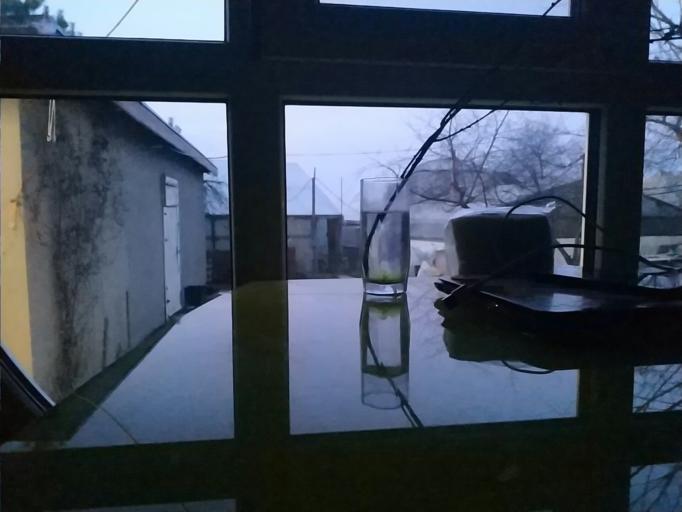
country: RU
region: Republic of Karelia
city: Sukkozero
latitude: 62.8249
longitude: 31.8327
